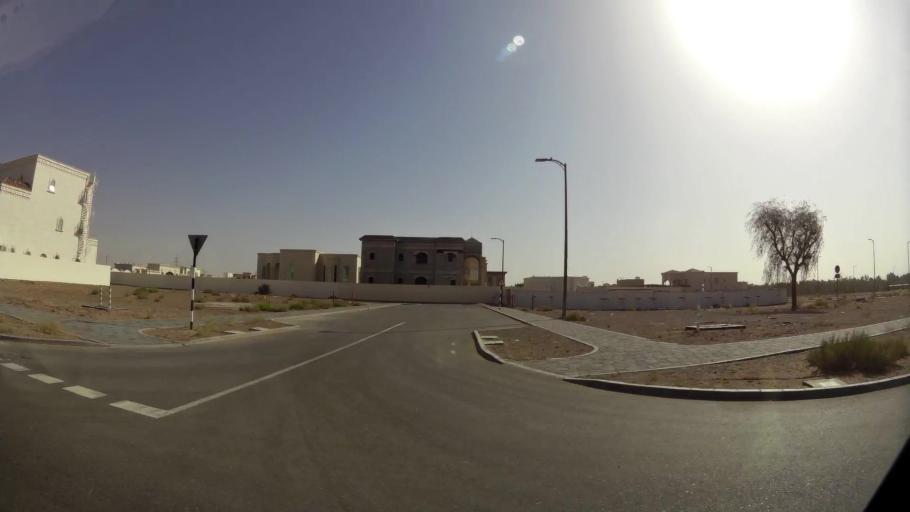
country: OM
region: Al Buraimi
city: Al Buraymi
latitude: 24.3588
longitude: 55.7909
